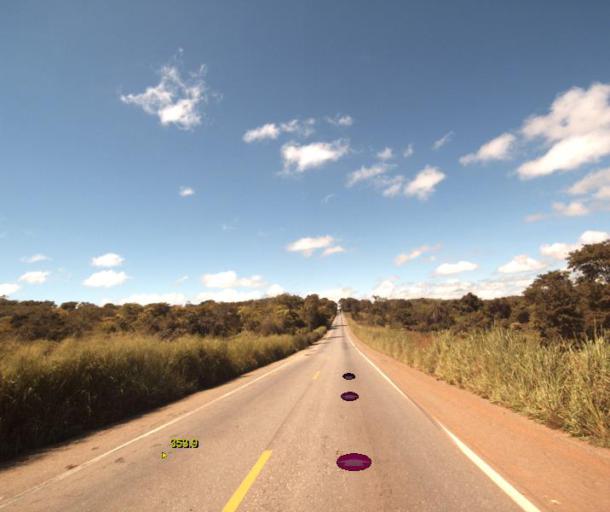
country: BR
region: Goias
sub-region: Jaragua
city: Jaragua
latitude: -15.6882
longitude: -49.3391
